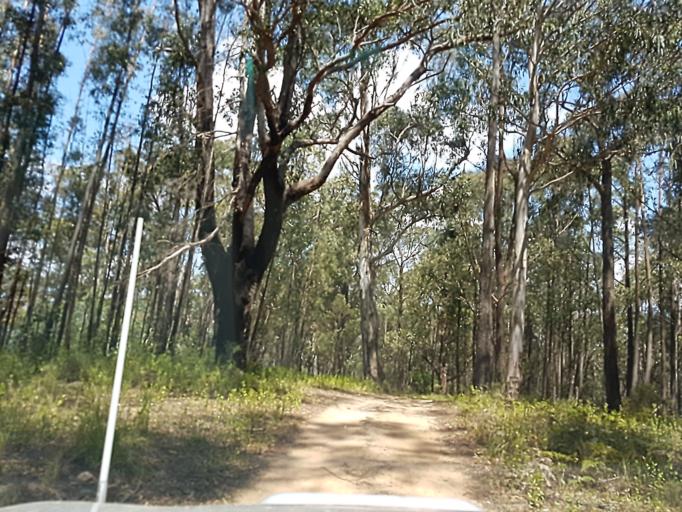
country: AU
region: Victoria
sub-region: East Gippsland
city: Lakes Entrance
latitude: -37.3955
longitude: 148.2970
